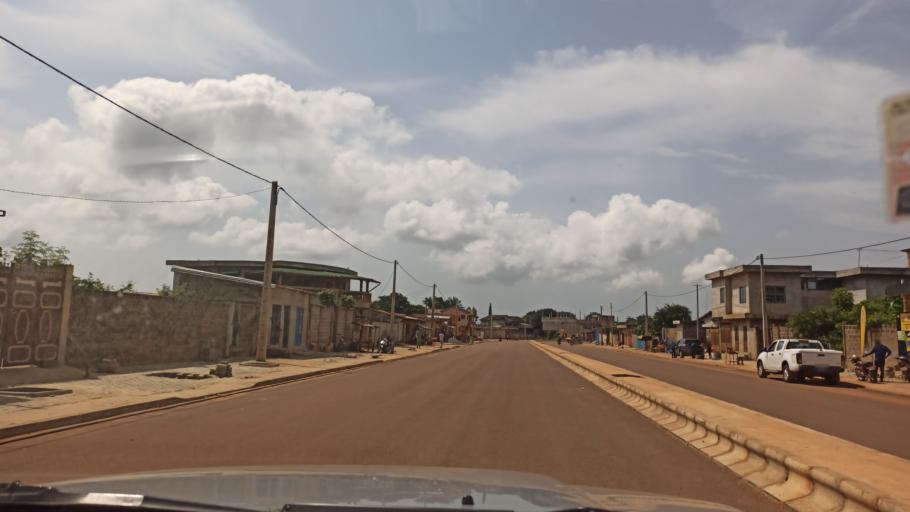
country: BJ
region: Queme
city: Porto-Novo
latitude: 6.4844
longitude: 2.5965
